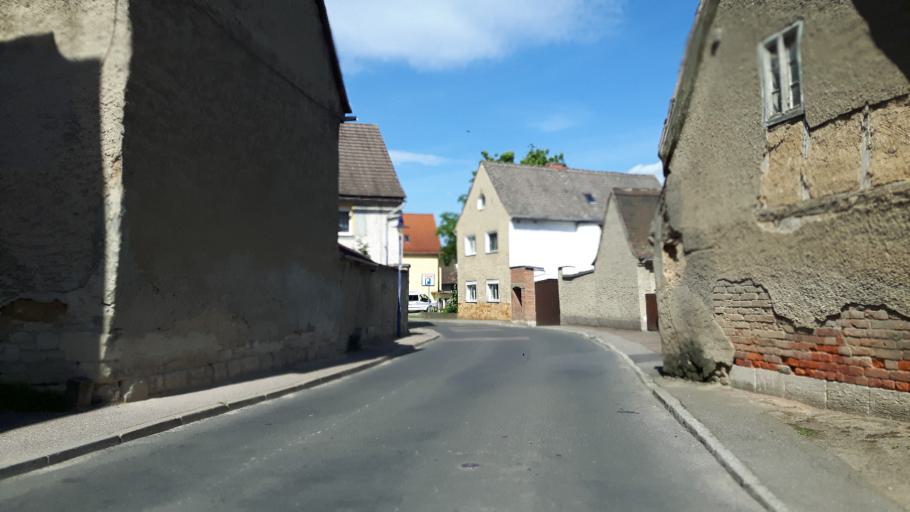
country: DE
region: Saxony-Anhalt
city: Bad Kosen
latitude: 51.1153
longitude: 11.7117
